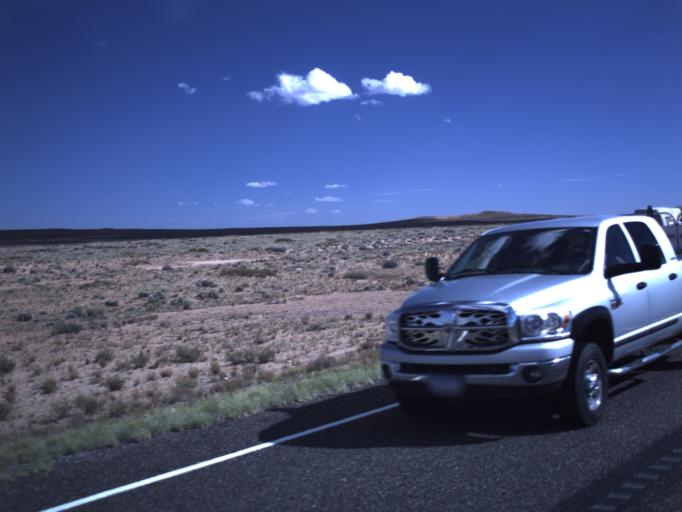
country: US
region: Utah
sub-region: Wayne County
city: Loa
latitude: 38.1765
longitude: -110.6252
